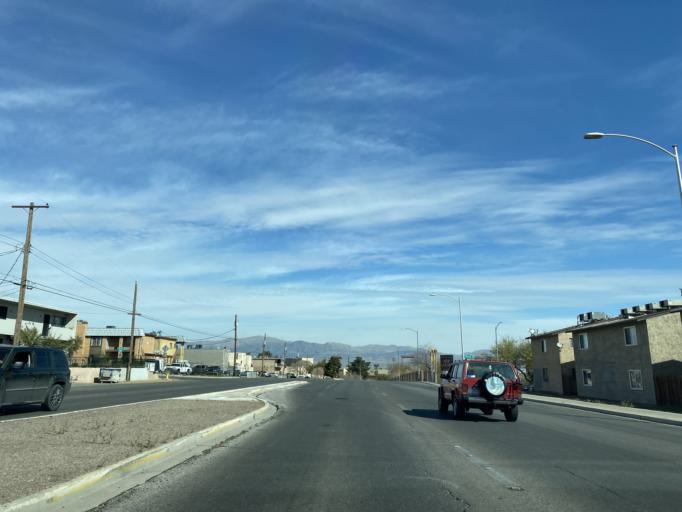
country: US
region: Nevada
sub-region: Clark County
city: Las Vegas
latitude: 36.1750
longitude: -115.1305
